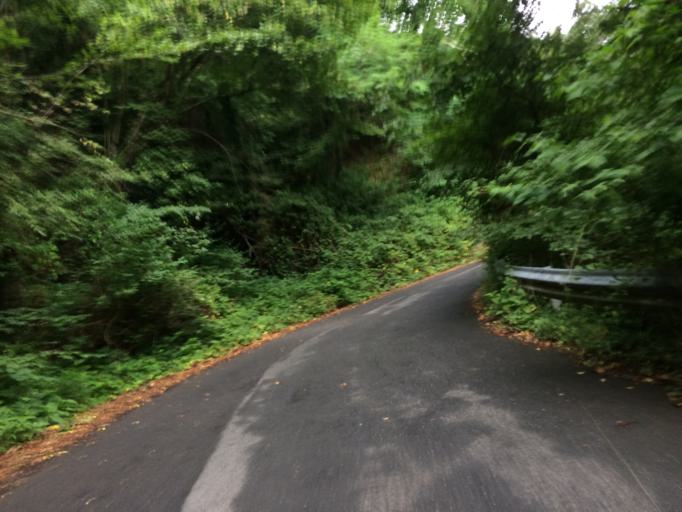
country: IT
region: Liguria
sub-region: Provincia di Imperia
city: Triora
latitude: 43.9864
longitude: 7.7596
